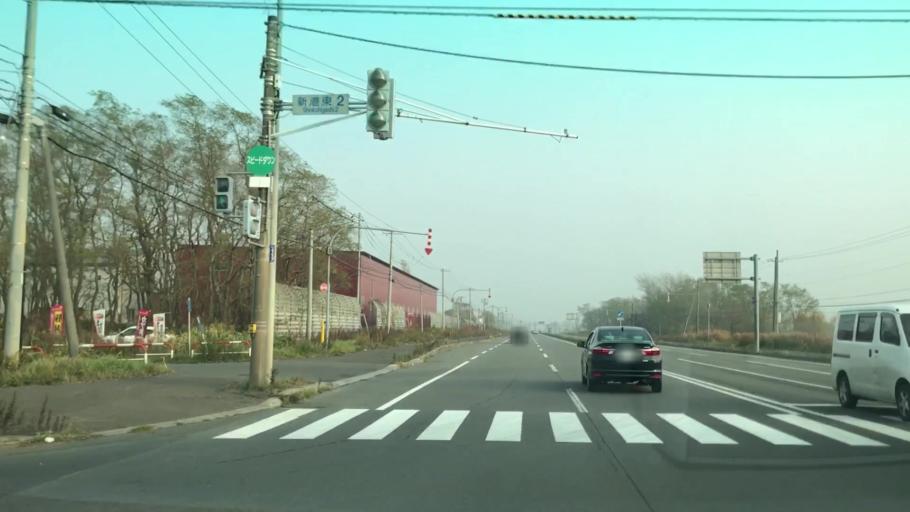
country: JP
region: Hokkaido
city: Ishikari
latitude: 43.2085
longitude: 141.3332
